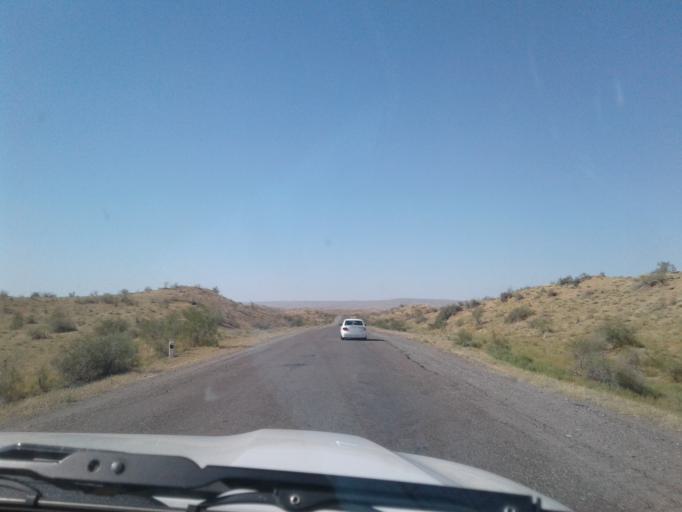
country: TM
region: Mary
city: Yoloeten
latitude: 36.4301
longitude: 62.5827
